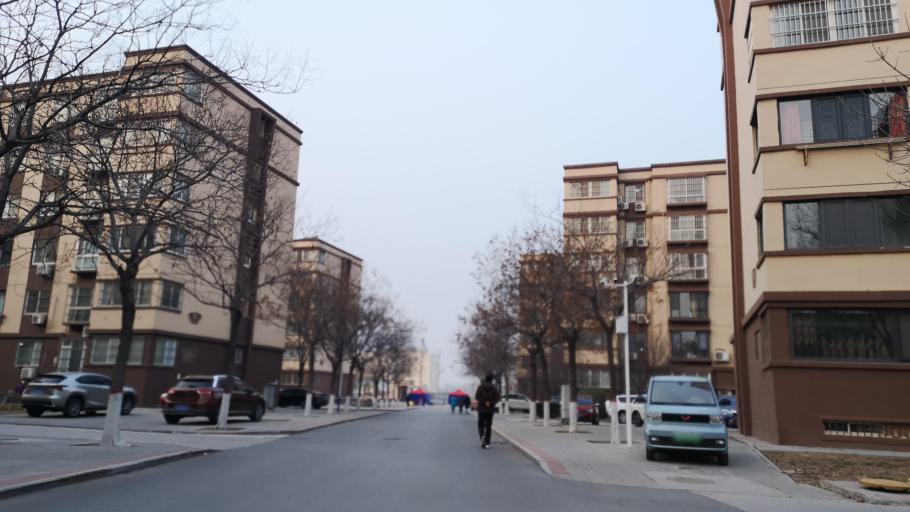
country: CN
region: Henan Sheng
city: Zhongyuanlu
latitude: 35.7881
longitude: 115.0786
